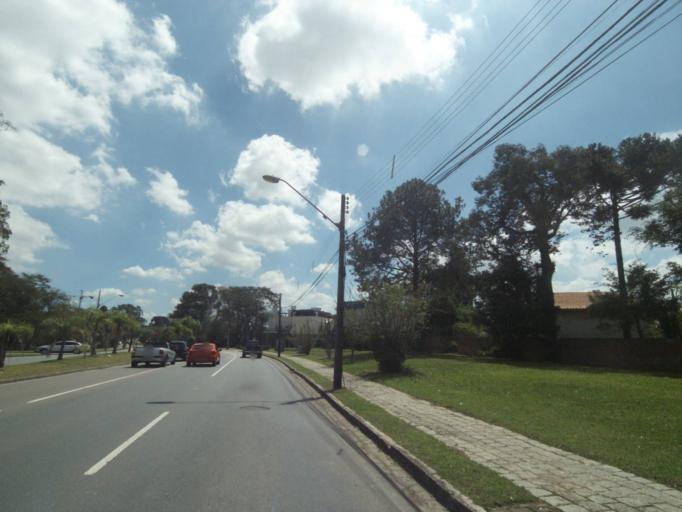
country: BR
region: Parana
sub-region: Curitiba
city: Curitiba
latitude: -25.4138
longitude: -49.2410
